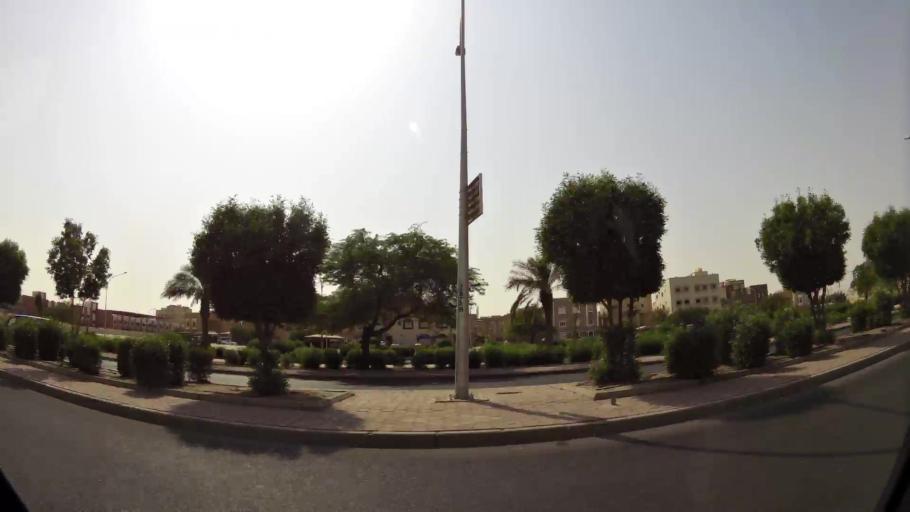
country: KW
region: Muhafazat al Jahra'
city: Al Jahra'
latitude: 29.3373
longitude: 47.6948
